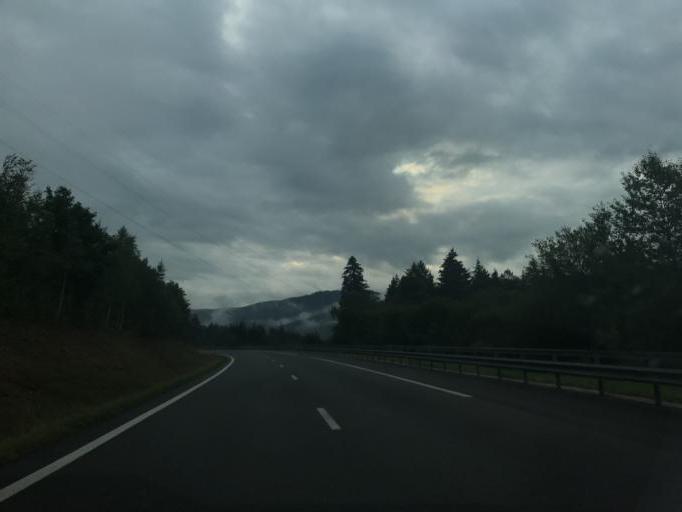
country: FR
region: Rhone-Alpes
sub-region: Departement de l'Ain
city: Montreal-la-Cluse
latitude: 46.1946
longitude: 5.5810
